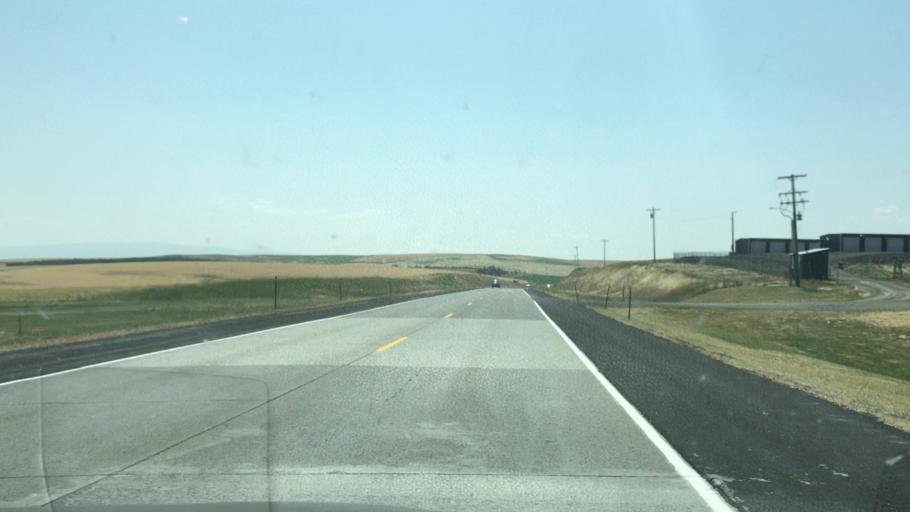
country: US
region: Idaho
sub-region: Lewis County
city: Nezperce
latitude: 46.0775
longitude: -116.3432
